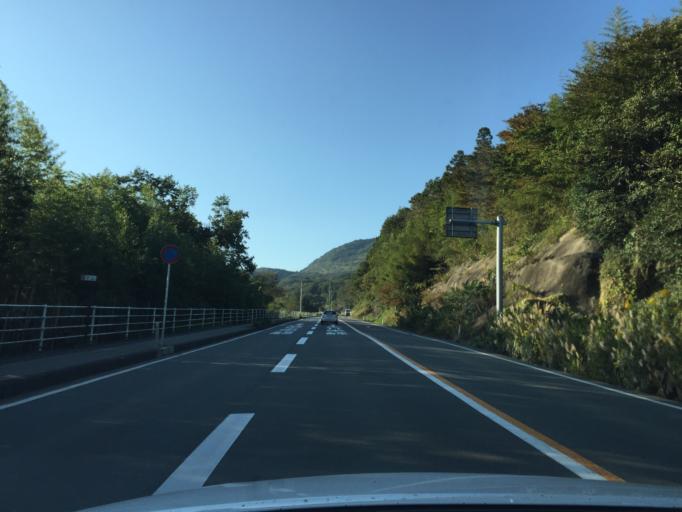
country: JP
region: Fukushima
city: Iwaki
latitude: 37.0769
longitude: 140.8193
